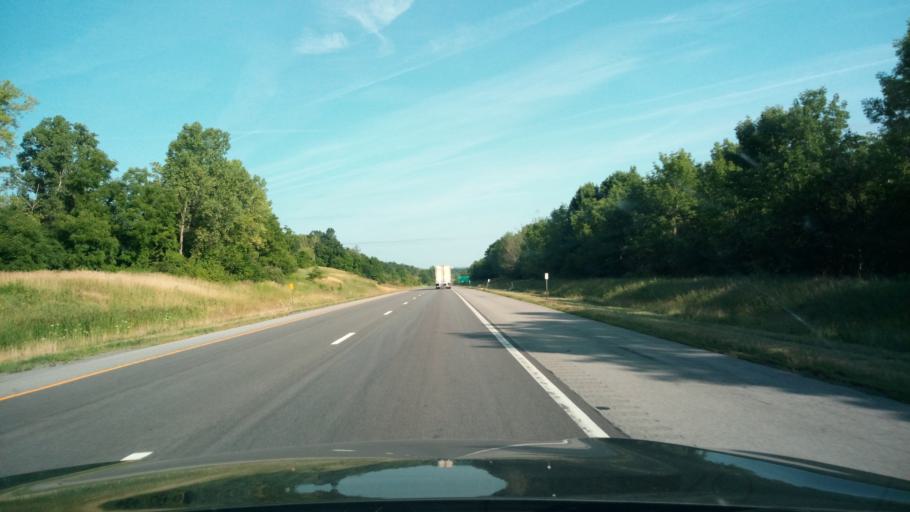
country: US
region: New York
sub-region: Livingston County
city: Mount Morris
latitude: 42.6459
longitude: -77.7938
